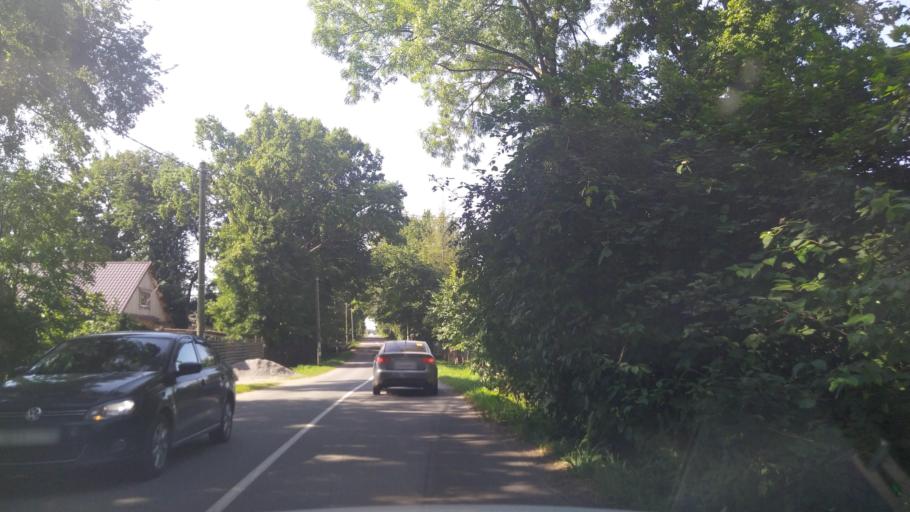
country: RU
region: Leningrad
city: Siverskiy
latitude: 59.2911
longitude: 30.0650
